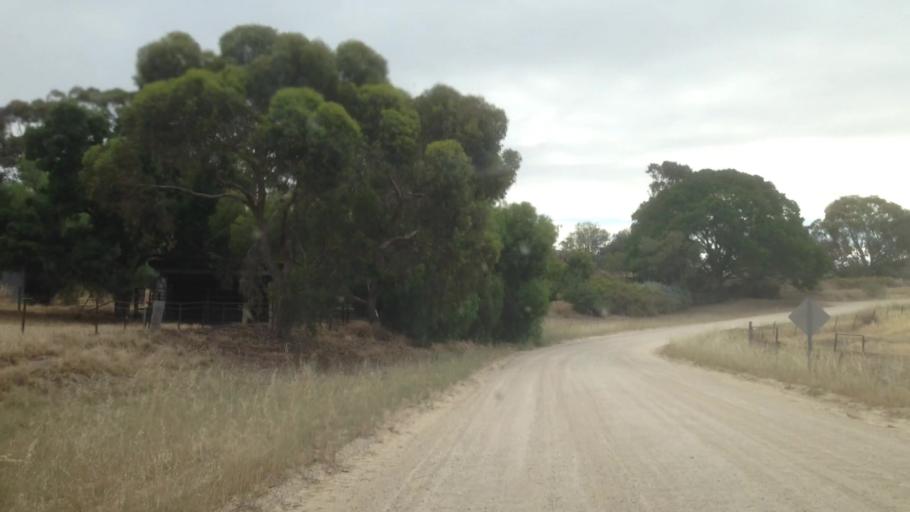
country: AU
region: South Australia
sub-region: Barossa
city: Lyndoch
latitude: -34.6002
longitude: 138.9454
